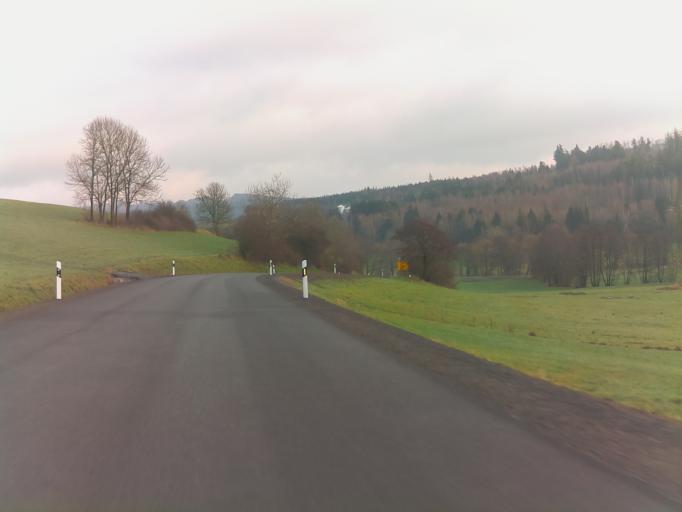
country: DE
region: Hesse
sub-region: Regierungsbezirk Kassel
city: Hilders
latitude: 50.5606
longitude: 9.9304
